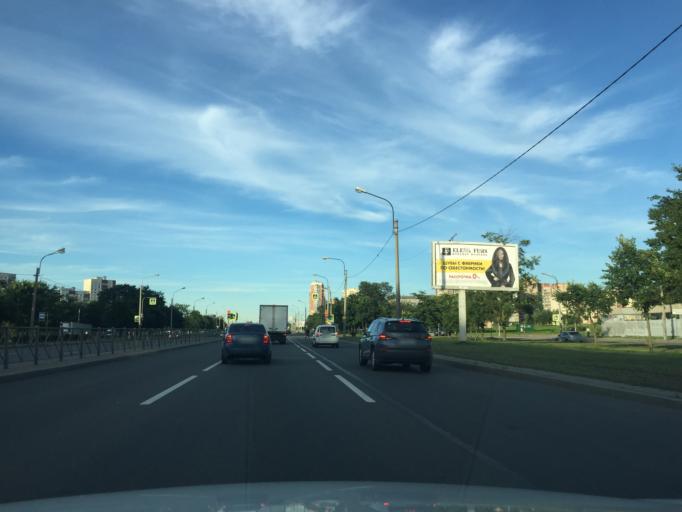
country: RU
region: St.-Petersburg
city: Shushary
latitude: 59.8403
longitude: 30.4026
